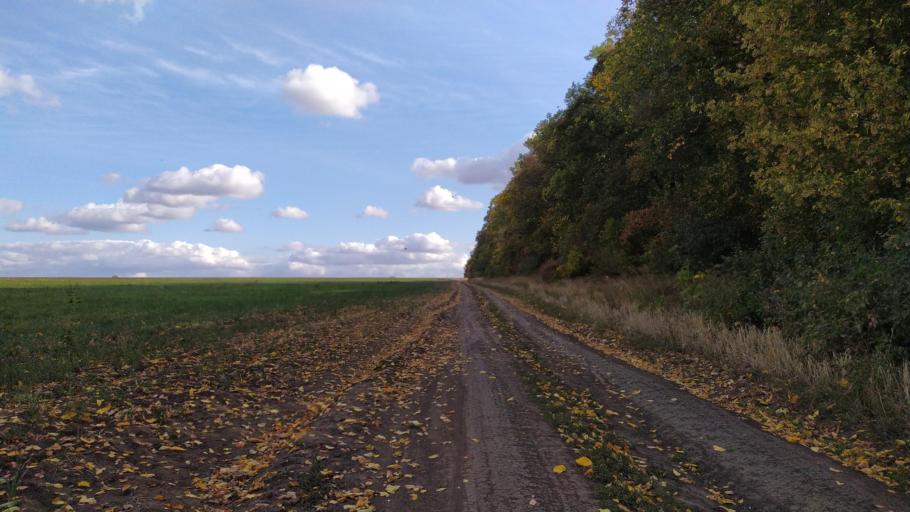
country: RU
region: Kursk
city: Kursk
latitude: 51.6197
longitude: 36.1625
